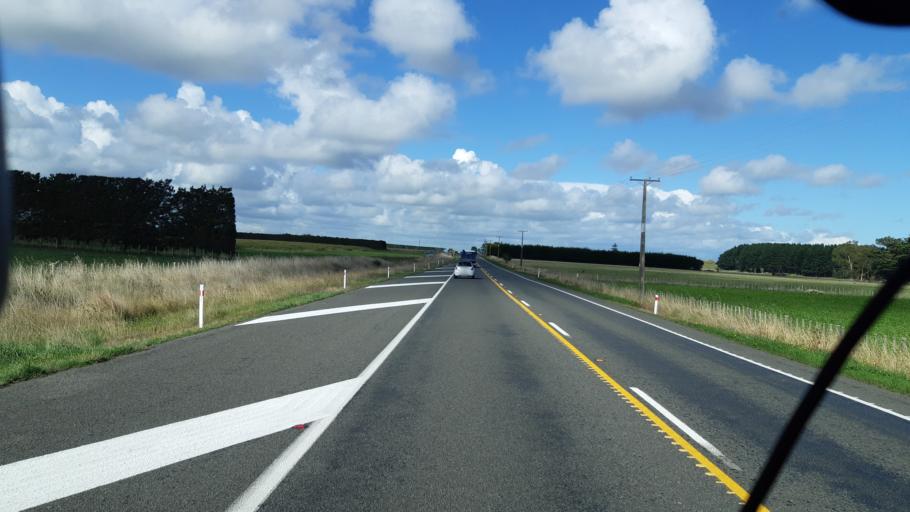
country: NZ
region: Manawatu-Wanganui
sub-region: Wanganui District
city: Wanganui
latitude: -39.9868
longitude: 175.1571
